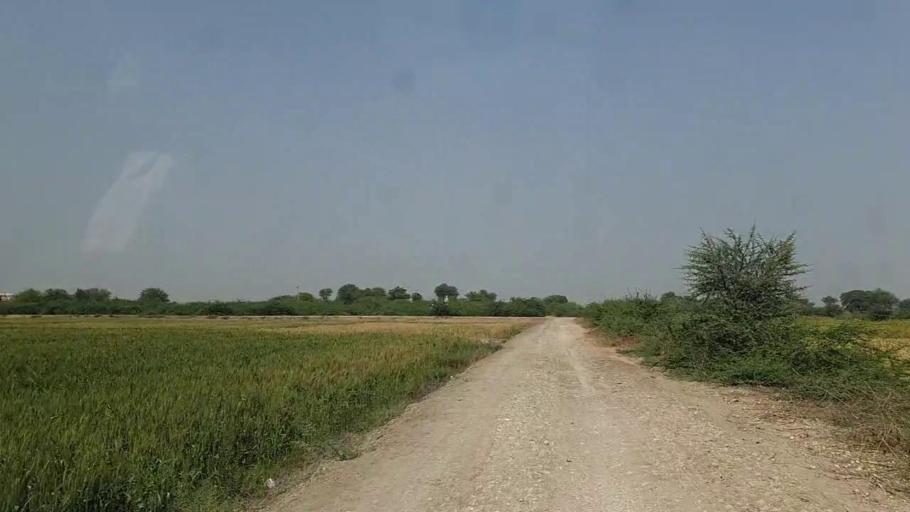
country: PK
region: Sindh
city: Naukot
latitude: 24.8114
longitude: 69.3755
